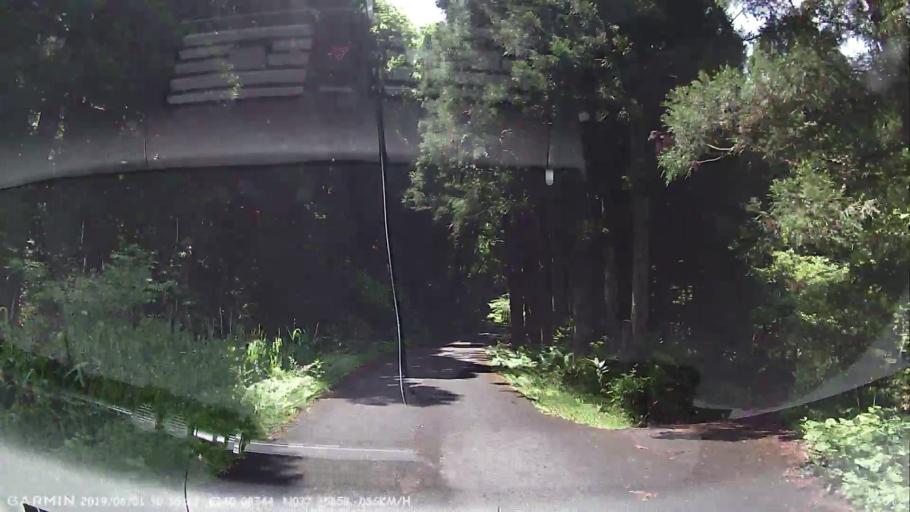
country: JP
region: Fukushima
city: Inawashiro
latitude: 37.3555
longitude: 140.0874
